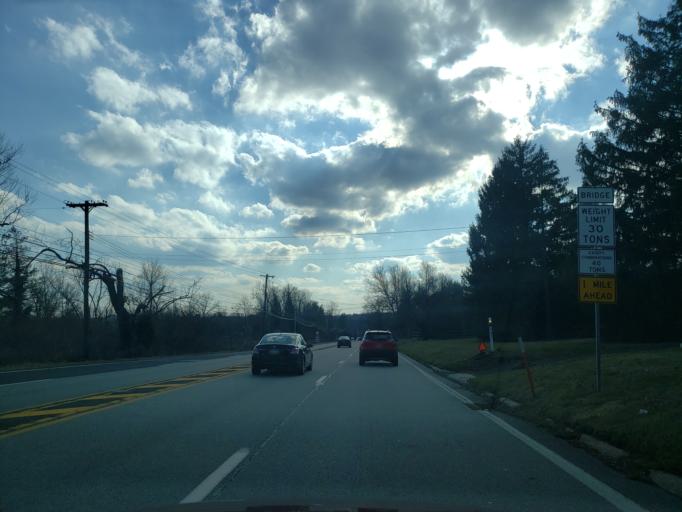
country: US
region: Pennsylvania
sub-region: Montgomery County
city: North Wales
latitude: 40.1988
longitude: -75.2569
